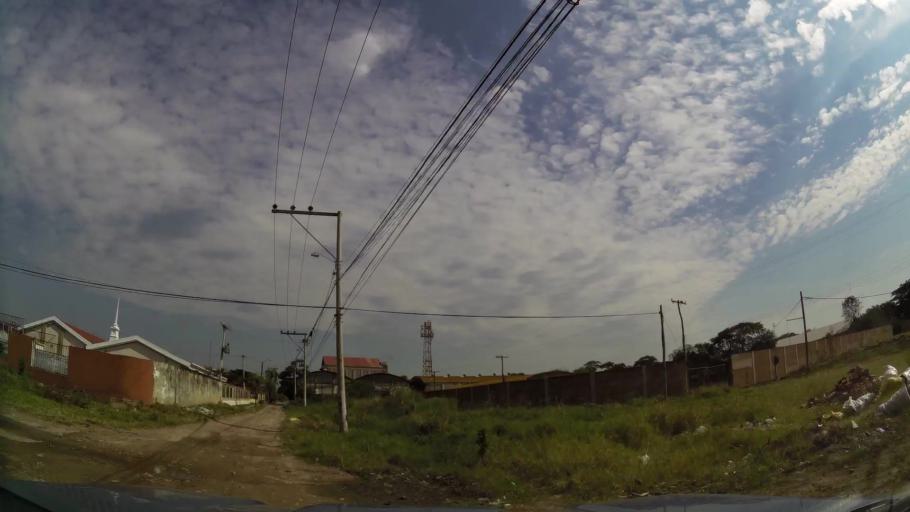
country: BO
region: Santa Cruz
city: Santa Cruz de la Sierra
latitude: -17.7283
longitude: -63.1682
